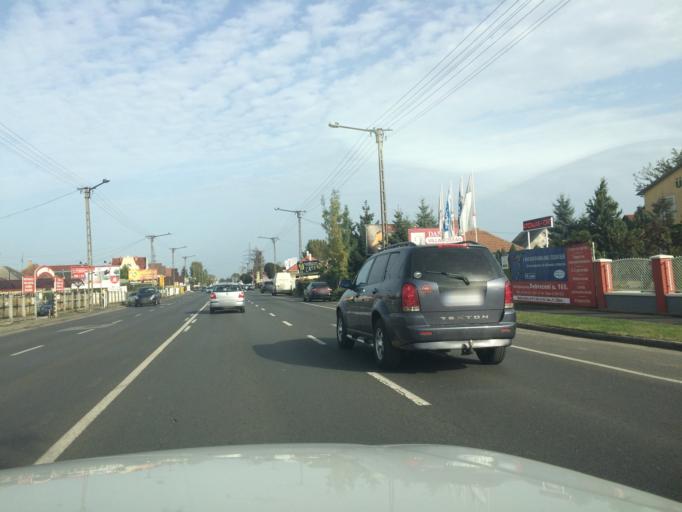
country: HU
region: Szabolcs-Szatmar-Bereg
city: Nyiregyhaza
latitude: 47.9286
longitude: 21.7187
